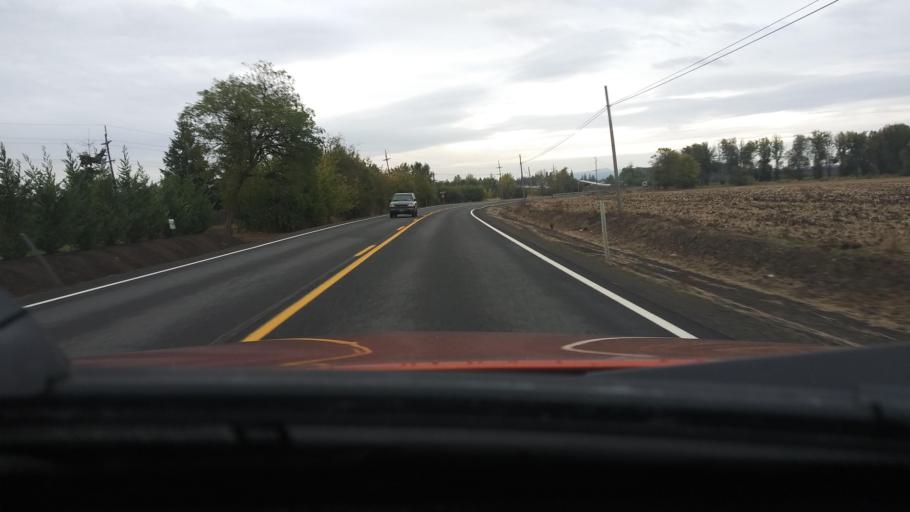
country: US
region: Oregon
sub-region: Washington County
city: Banks
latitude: 45.5766
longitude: -123.1103
